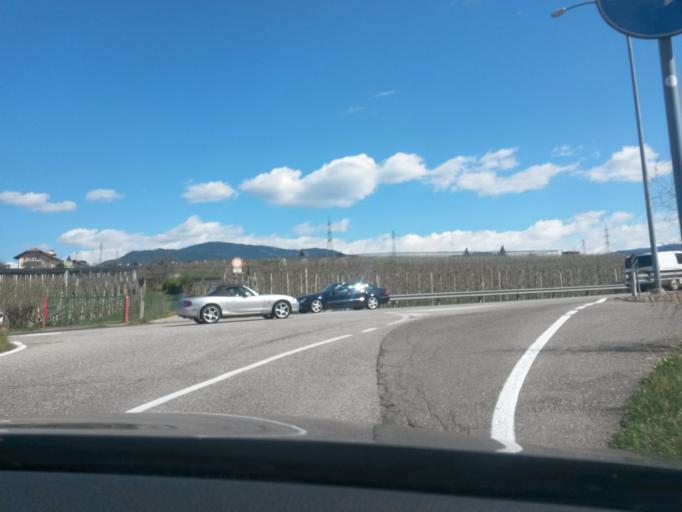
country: IT
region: Trentino-Alto Adige
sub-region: Bolzano
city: San Michele
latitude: 46.4579
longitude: 11.2683
